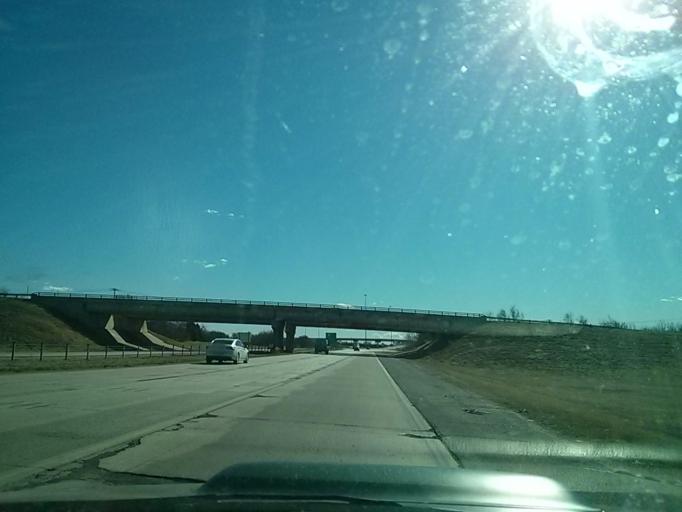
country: US
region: Oklahoma
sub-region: Tulsa County
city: Turley
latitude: 36.2073
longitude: -95.9466
